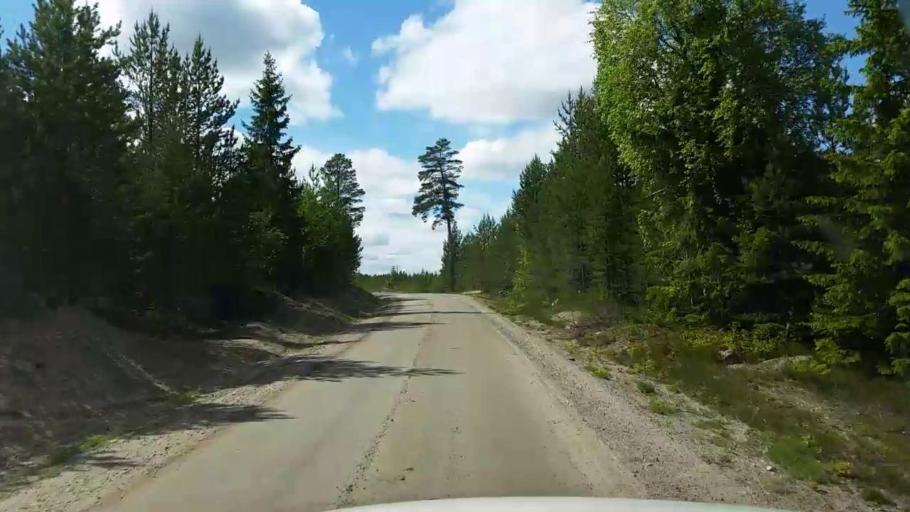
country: SE
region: Gaevleborg
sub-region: Ovanakers Kommun
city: Edsbyn
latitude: 61.5722
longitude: 15.9315
